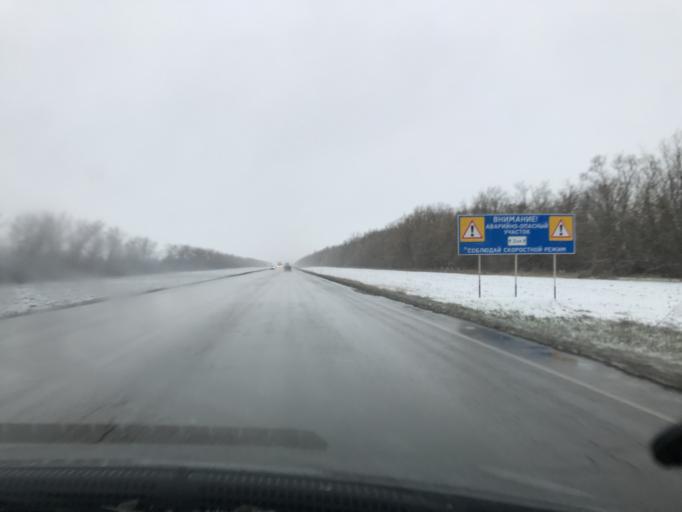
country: RU
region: Rostov
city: Yegorlykskaya
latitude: 46.6432
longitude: 40.5768
